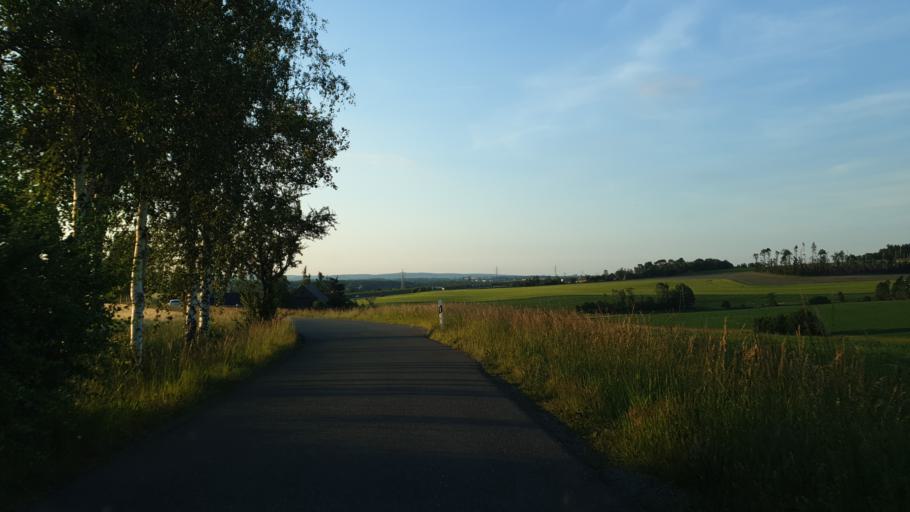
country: DE
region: Saxony
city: Oelsnitz
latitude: 50.6894
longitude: 12.7296
